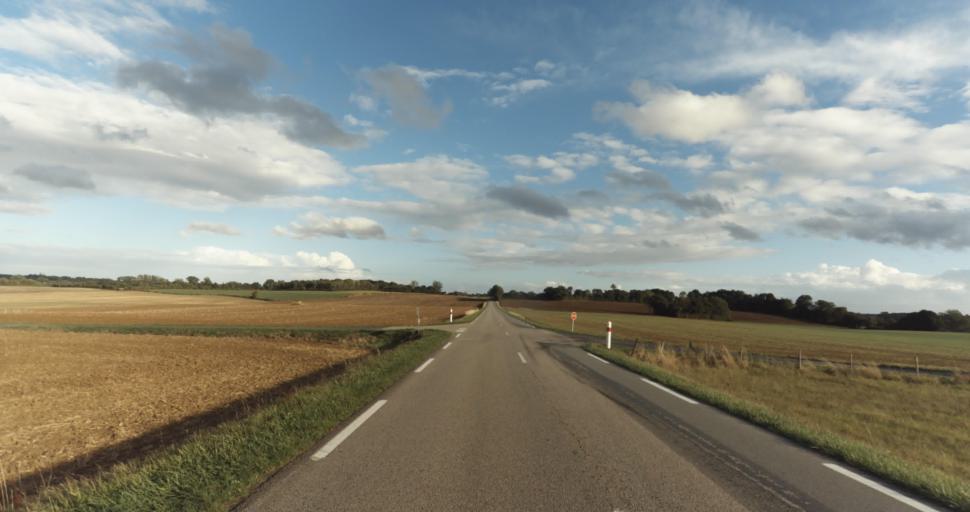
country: FR
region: Lower Normandy
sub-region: Departement de l'Orne
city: Sainte-Gauburge-Sainte-Colombe
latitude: 48.7328
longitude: 0.4007
